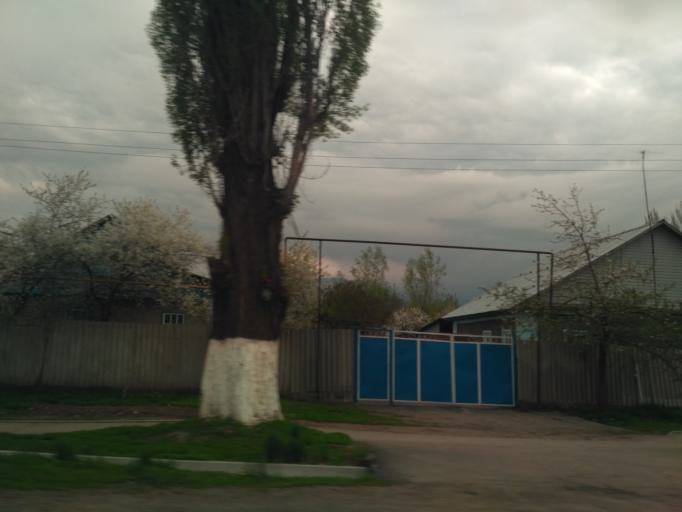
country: KZ
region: Almaty Oblysy
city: Burunday
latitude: 43.2107
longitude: 76.3268
